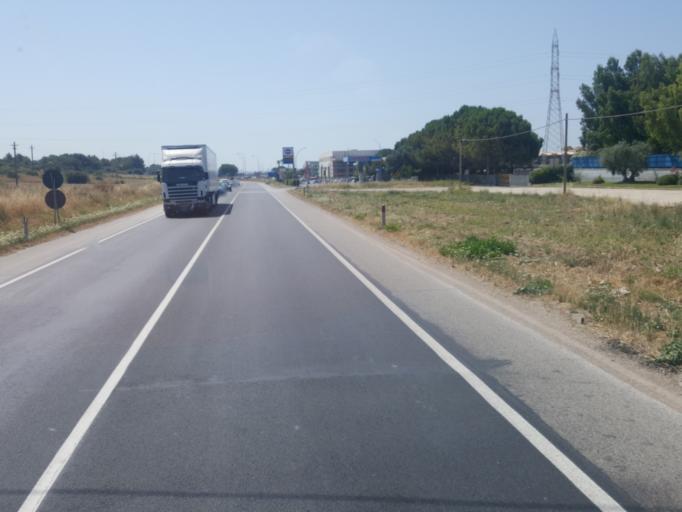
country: IT
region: Apulia
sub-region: Provincia di Taranto
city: Massafra
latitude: 40.5643
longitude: 17.1298
